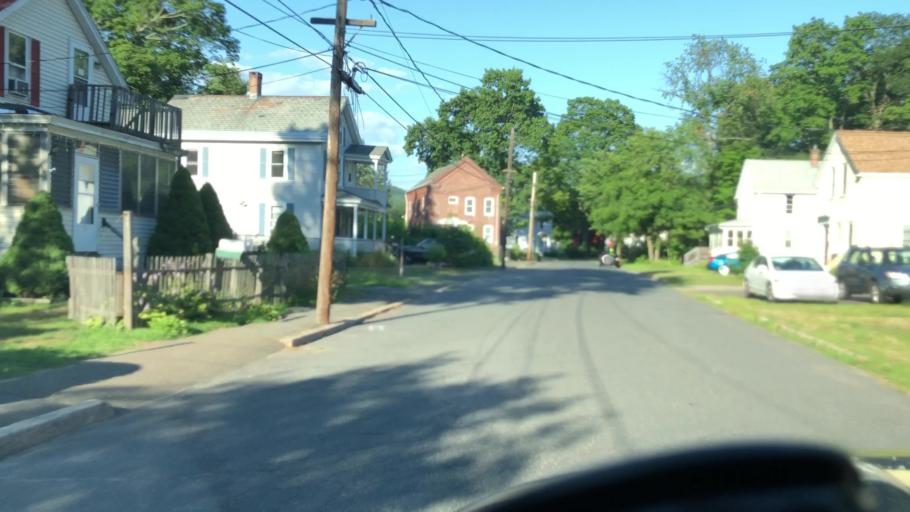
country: US
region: Massachusetts
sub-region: Hampshire County
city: Easthampton
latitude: 42.2624
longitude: -72.6640
